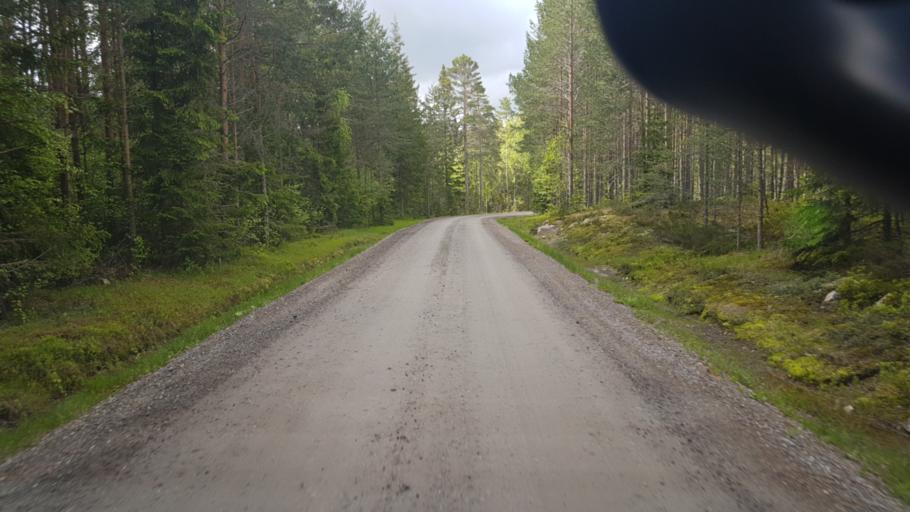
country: NO
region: Ostfold
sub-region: Romskog
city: Romskog
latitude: 59.7141
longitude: 12.0162
